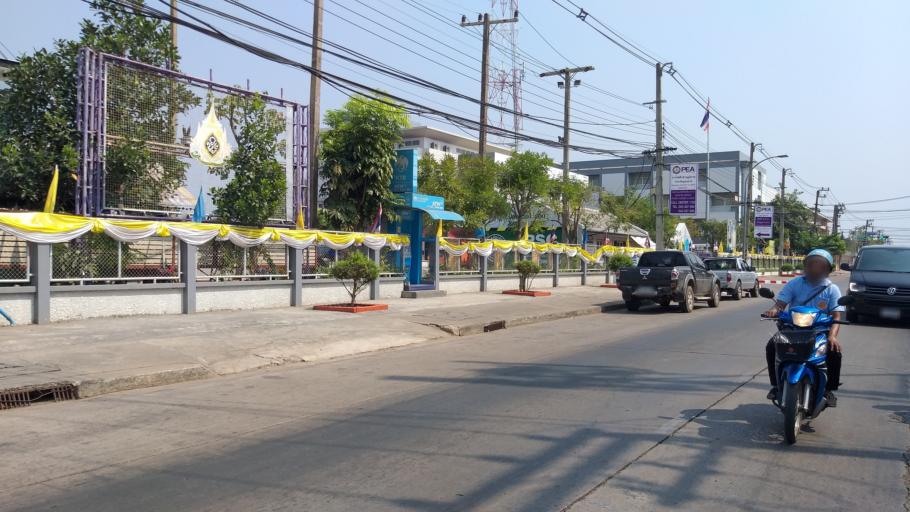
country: TH
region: Changwat Udon Thani
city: Udon Thani
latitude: 17.4060
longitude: 102.7794
